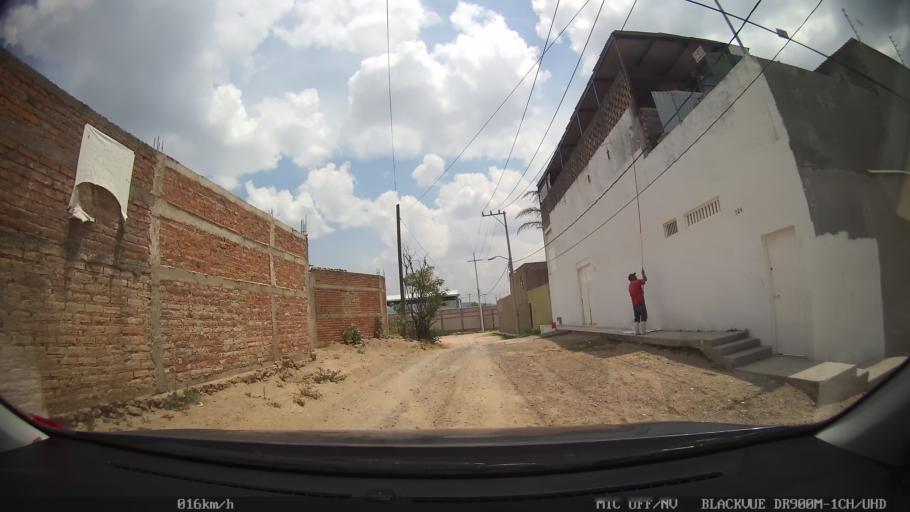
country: MX
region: Jalisco
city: Tonala
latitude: 20.6720
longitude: -103.2293
